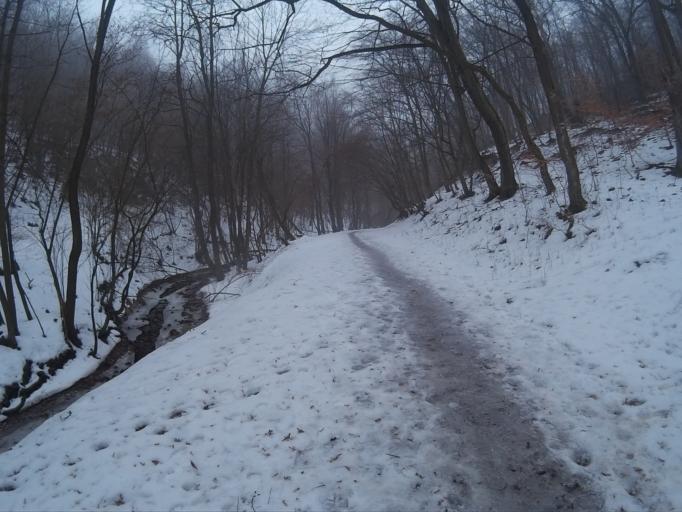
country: HU
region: Nograd
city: Matraverebely
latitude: 48.0011
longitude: 19.7594
